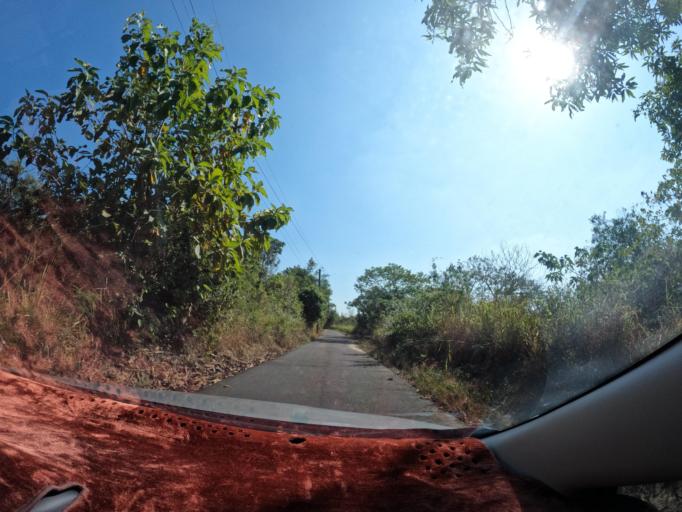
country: TW
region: Taiwan
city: Yujing
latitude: 23.0485
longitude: 120.3699
